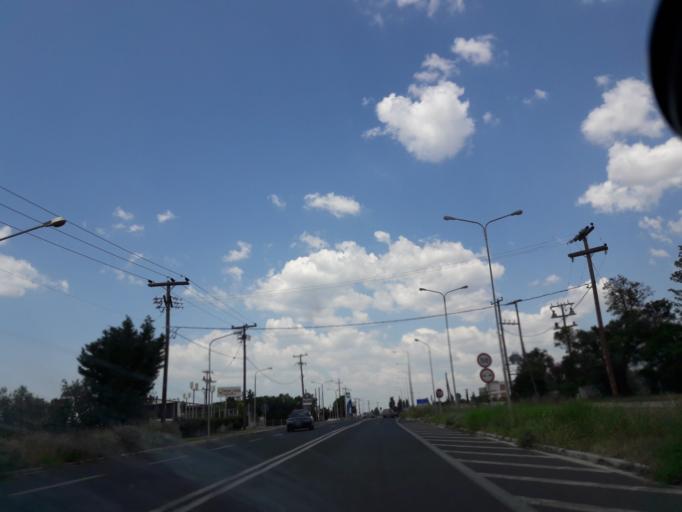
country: GR
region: Central Macedonia
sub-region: Nomos Thessalonikis
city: Thermi
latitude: 40.5309
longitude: 23.0419
